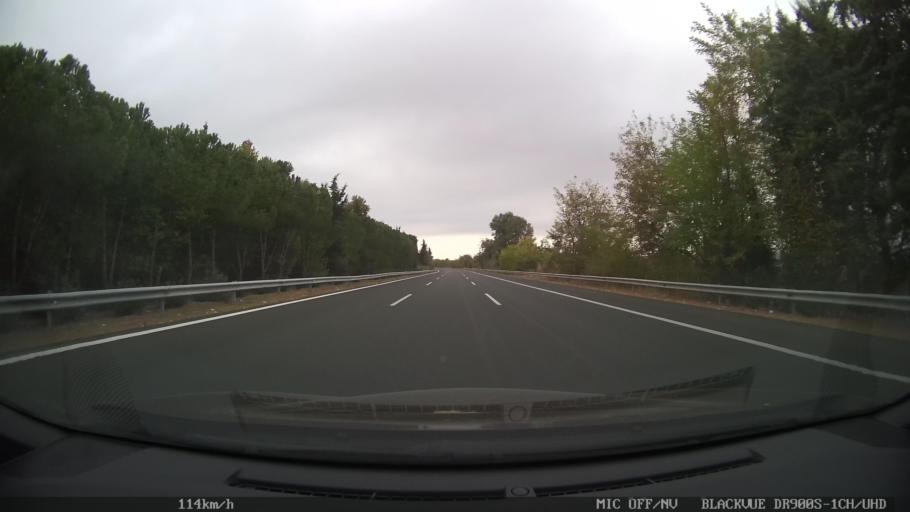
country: GR
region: Central Macedonia
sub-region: Nomos Pierias
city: Aiginio
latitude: 40.4999
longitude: 22.5655
